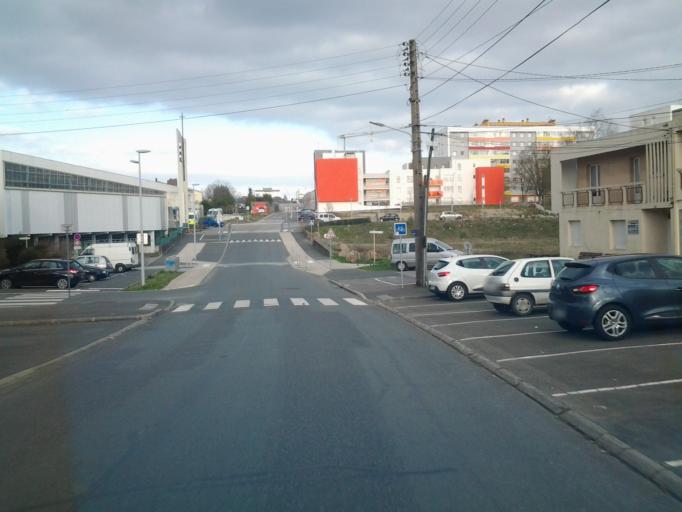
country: FR
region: Pays de la Loire
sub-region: Departement de la Vendee
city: La Roche-sur-Yon
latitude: 46.6794
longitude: -1.4422
